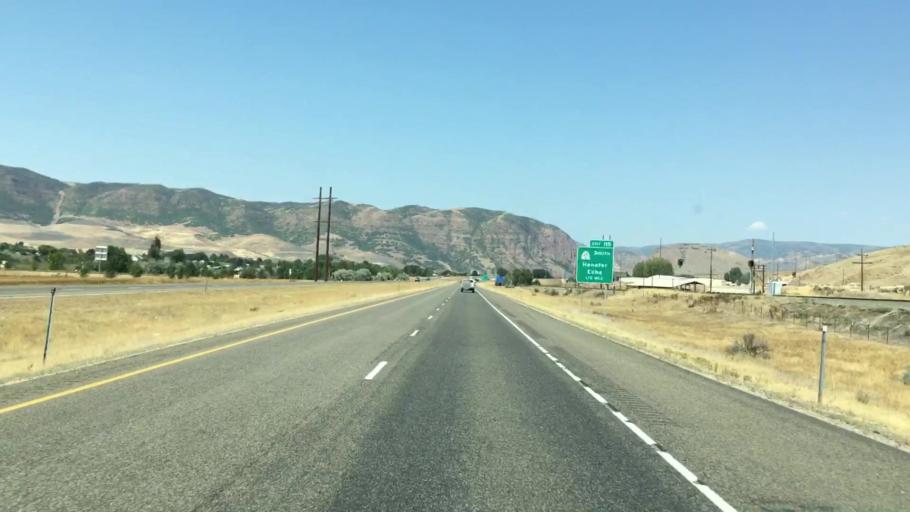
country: US
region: Utah
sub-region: Summit County
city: Coalville
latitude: 41.0086
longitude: -111.4770
